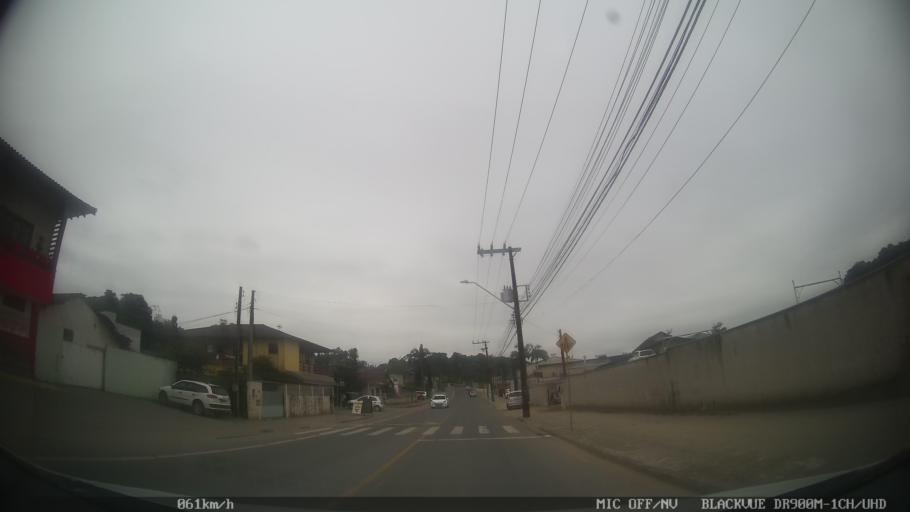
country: BR
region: Santa Catarina
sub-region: Joinville
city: Joinville
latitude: -26.3597
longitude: -48.8182
